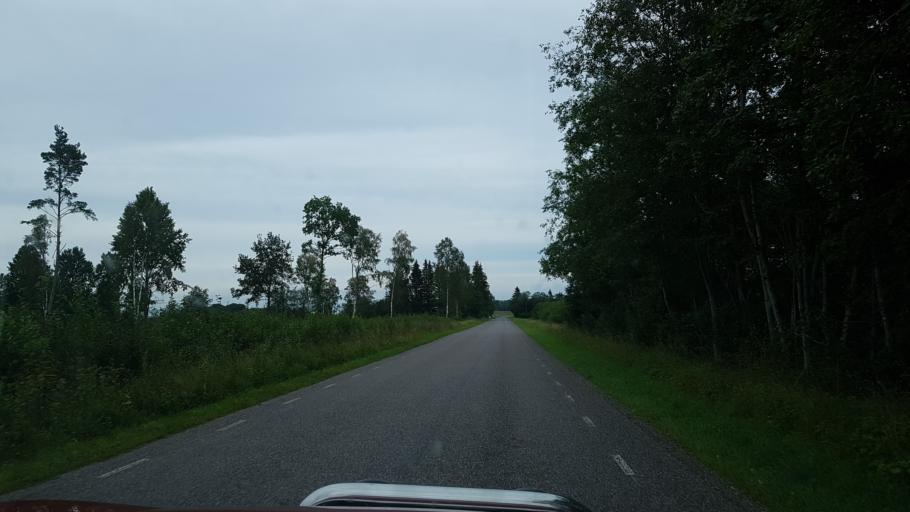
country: EE
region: Laeaene
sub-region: Lihula vald
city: Lihula
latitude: 58.8801
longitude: 23.8251
